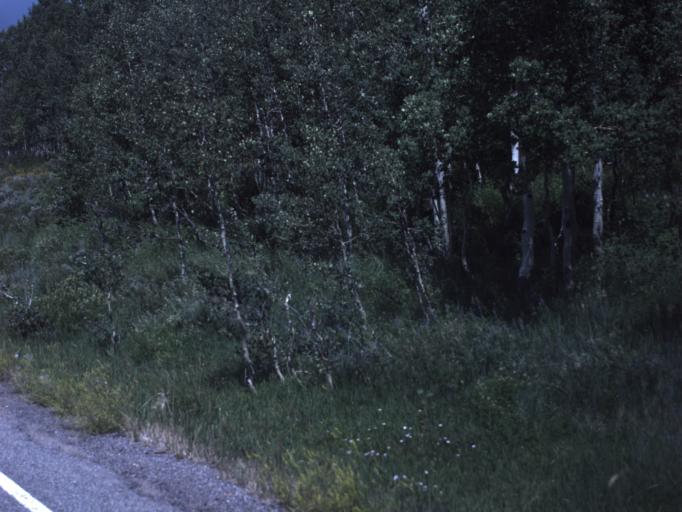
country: US
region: Utah
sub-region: Sanpete County
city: Fairview
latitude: 39.6564
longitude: -111.2988
